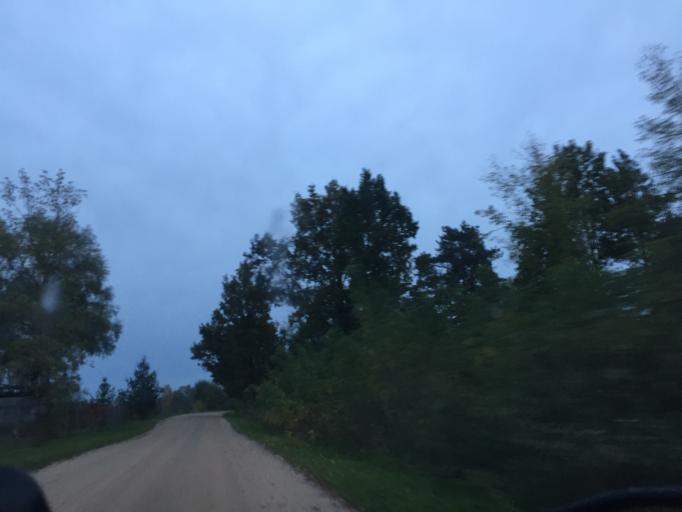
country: LV
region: Adazi
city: Adazi
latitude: 57.0811
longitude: 24.3683
